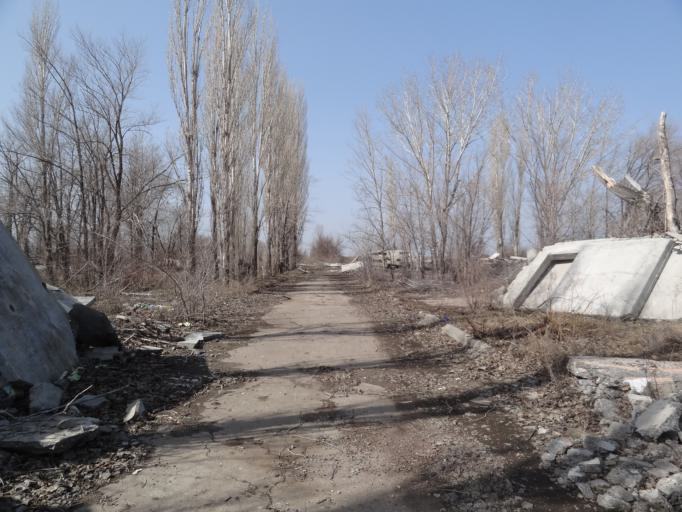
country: RU
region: Saratov
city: Engel's
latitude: 51.4360
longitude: 46.2256
